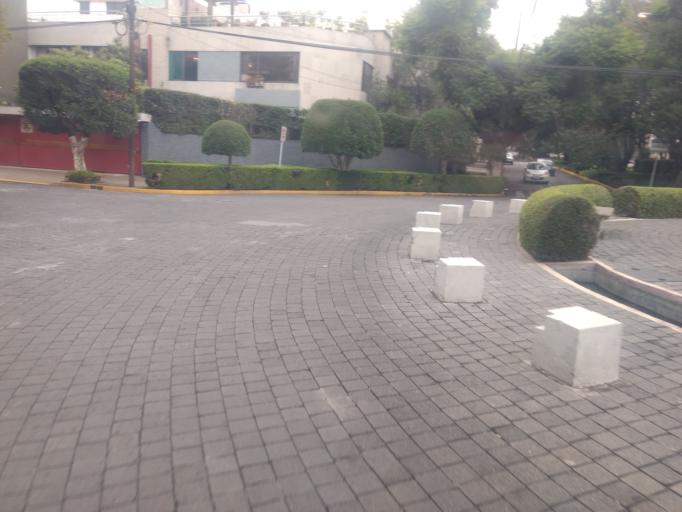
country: MX
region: Mexico City
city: Alvaro Obregon
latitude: 19.3679
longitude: -99.1839
